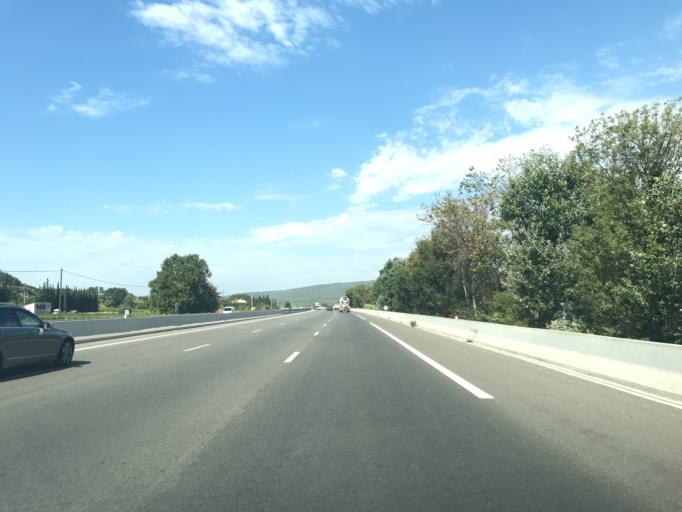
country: FR
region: Provence-Alpes-Cote d'Azur
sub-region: Departement du Var
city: Le Castellet
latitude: 43.2015
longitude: 5.7506
